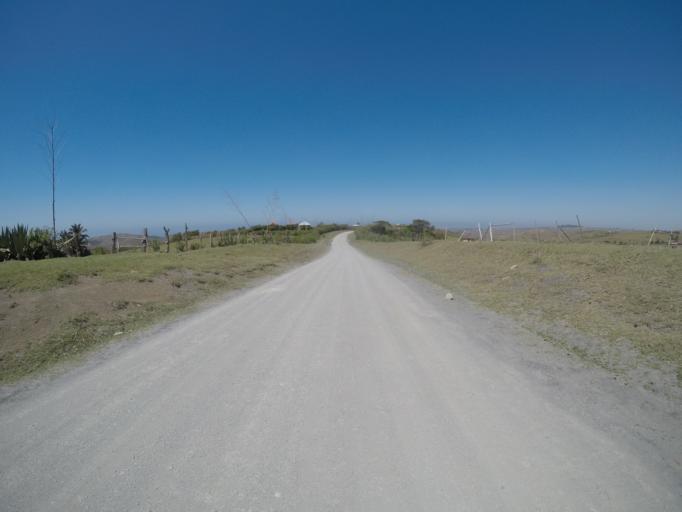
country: ZA
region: Eastern Cape
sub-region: OR Tambo District Municipality
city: Libode
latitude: -32.0040
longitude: 29.0723
